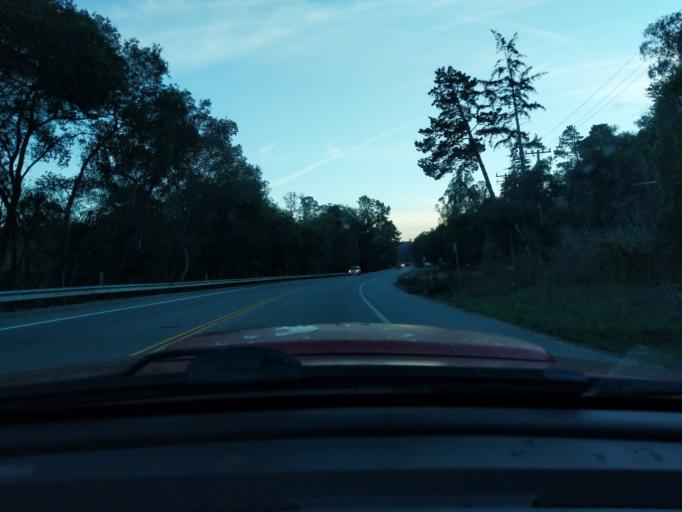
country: US
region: California
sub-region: Monterey County
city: Prunedale
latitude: 36.8201
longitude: -121.6729
